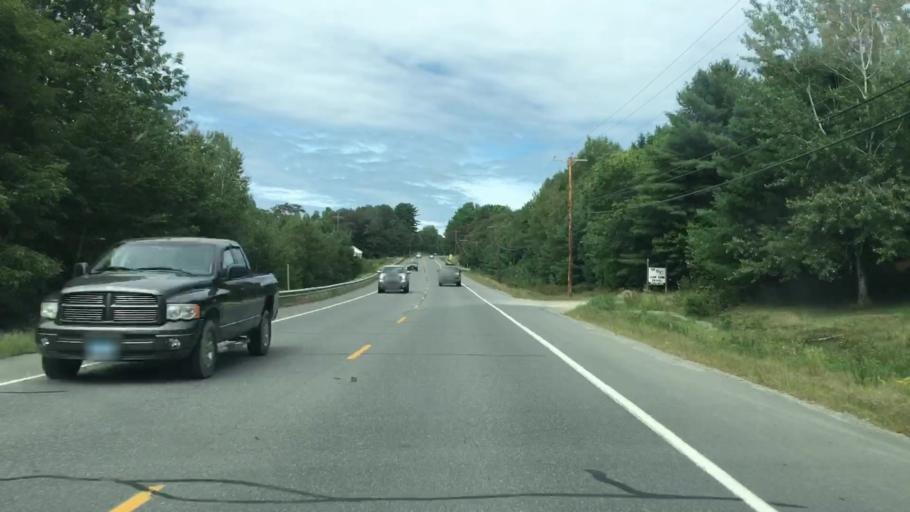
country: US
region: Maine
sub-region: Piscataquis County
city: Milo
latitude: 45.2772
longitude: -69.0048
